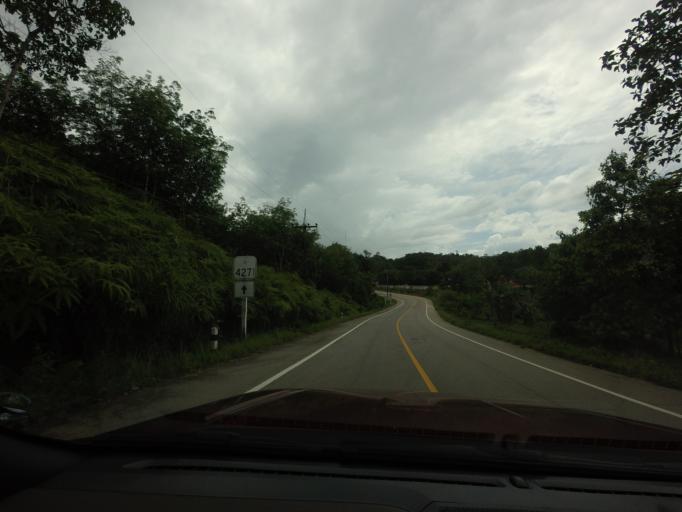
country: TH
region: Narathiwat
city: Sukhirin
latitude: 5.9782
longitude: 101.7048
